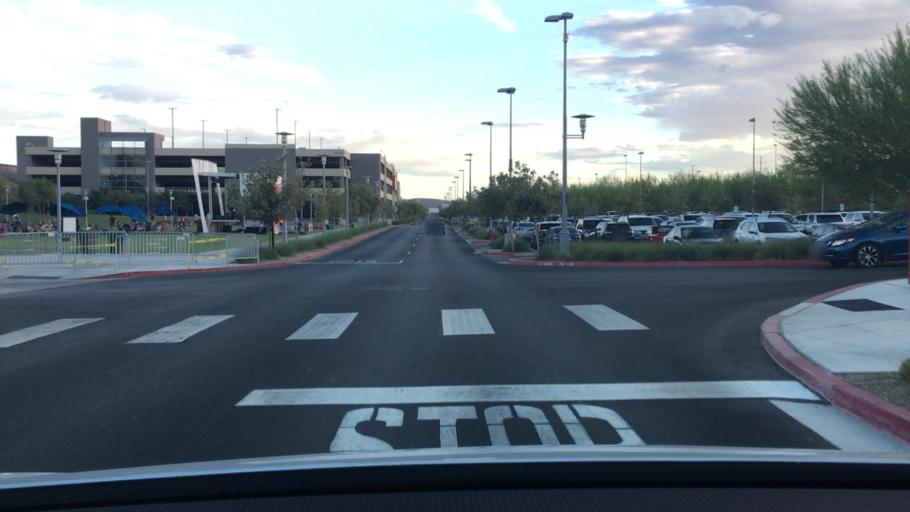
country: US
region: Nevada
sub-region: Clark County
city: Summerlin South
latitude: 36.1520
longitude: -115.3351
